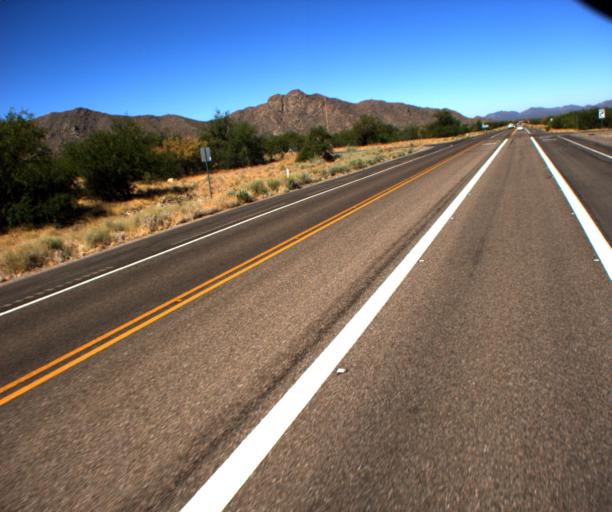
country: US
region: Arizona
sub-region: Pima County
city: Sells
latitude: 32.0157
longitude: -111.6343
